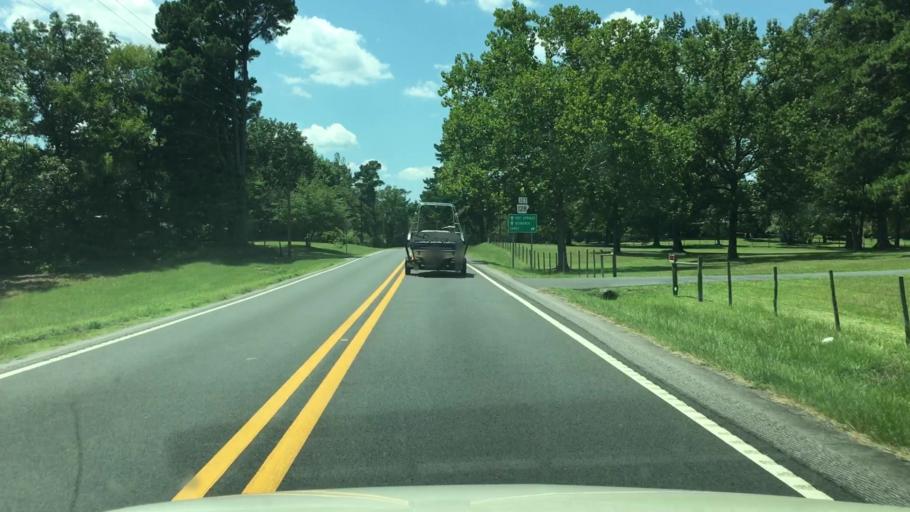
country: US
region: Arkansas
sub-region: Garland County
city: Lake Hamilton
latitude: 34.2649
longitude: -93.1337
